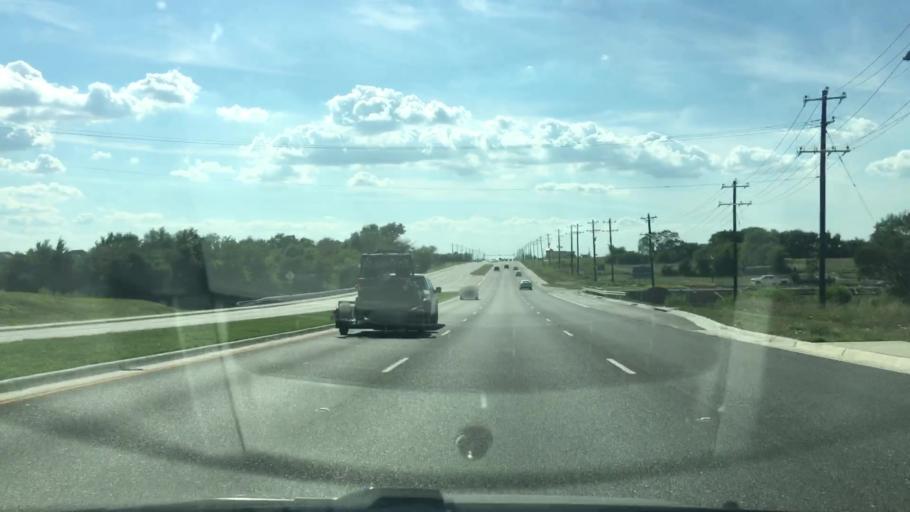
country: US
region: Texas
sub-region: Collin County
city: Prosper
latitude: 33.2187
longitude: -96.7550
